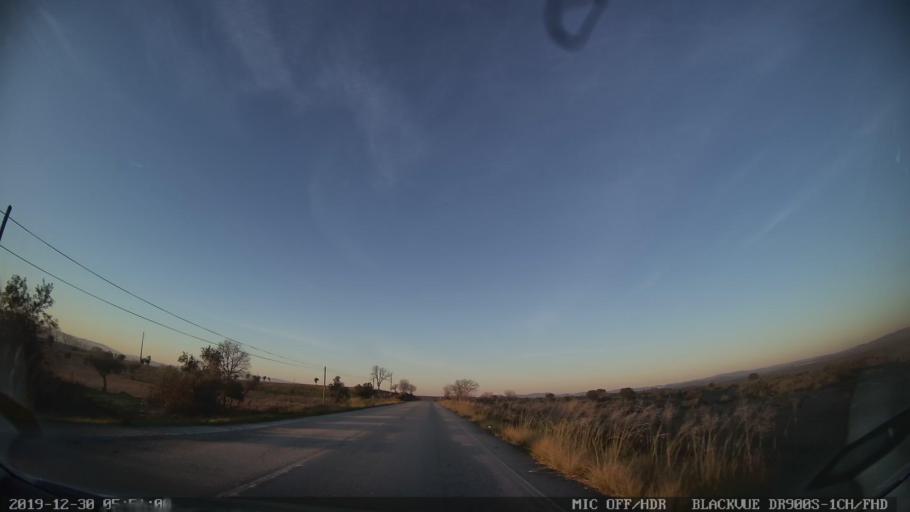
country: PT
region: Castelo Branco
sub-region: Idanha-A-Nova
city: Idanha-a-Nova
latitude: 39.9899
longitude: -7.2425
